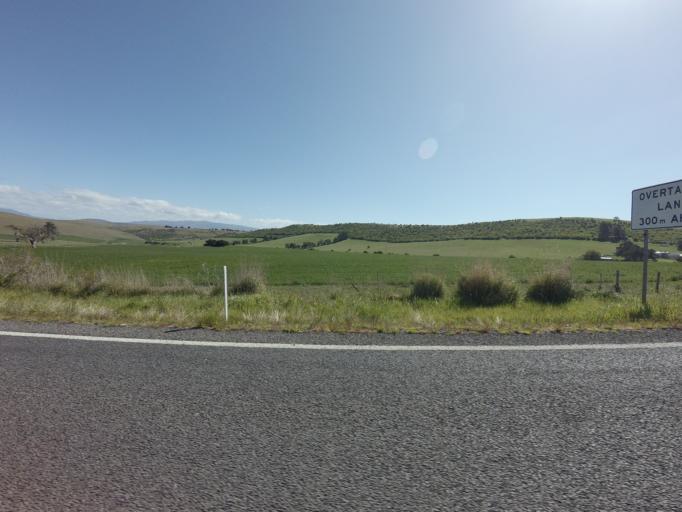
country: AU
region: Tasmania
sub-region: Derwent Valley
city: New Norfolk
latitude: -42.5676
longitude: 146.8809
